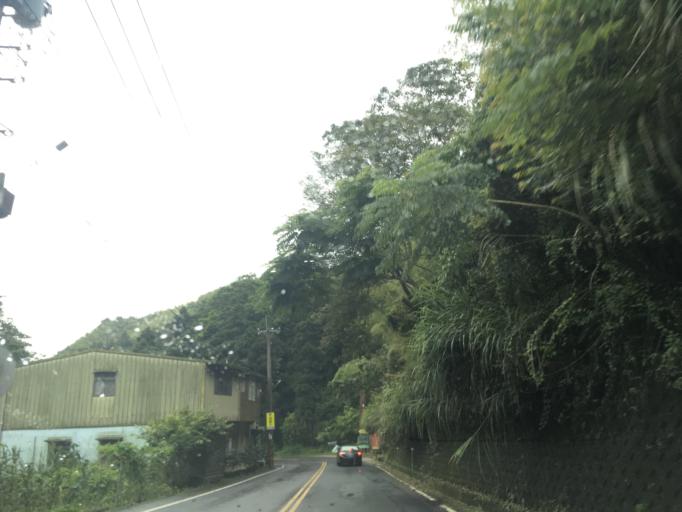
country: TW
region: Taiwan
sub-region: Yunlin
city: Douliu
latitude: 23.5603
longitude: 120.6073
